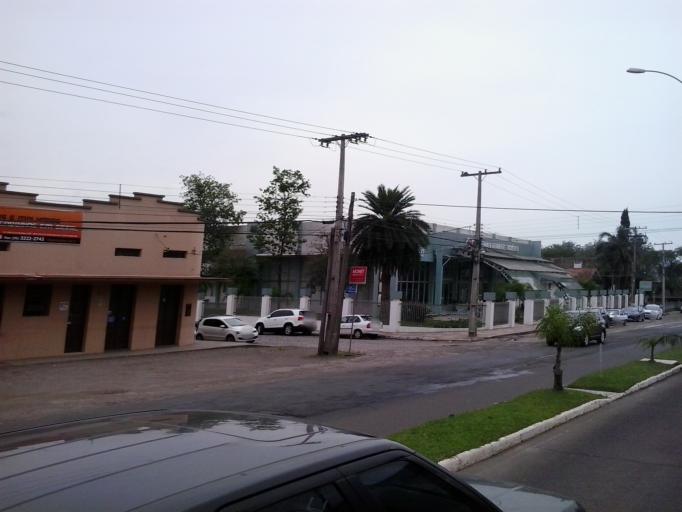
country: BR
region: Rio Grande do Sul
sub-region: Santa Maria
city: Santa Maria
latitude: -29.6947
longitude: -53.7786
